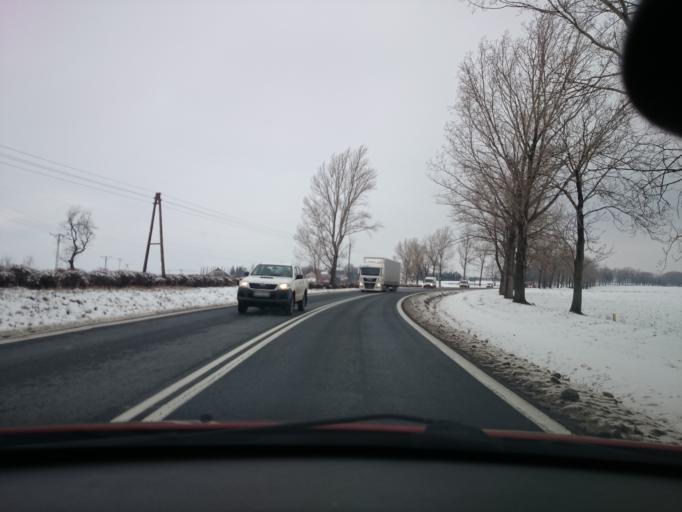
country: PL
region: Lower Silesian Voivodeship
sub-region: Powiat zabkowicki
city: Zabkowice Slaskie
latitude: 50.5674
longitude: 16.7891
